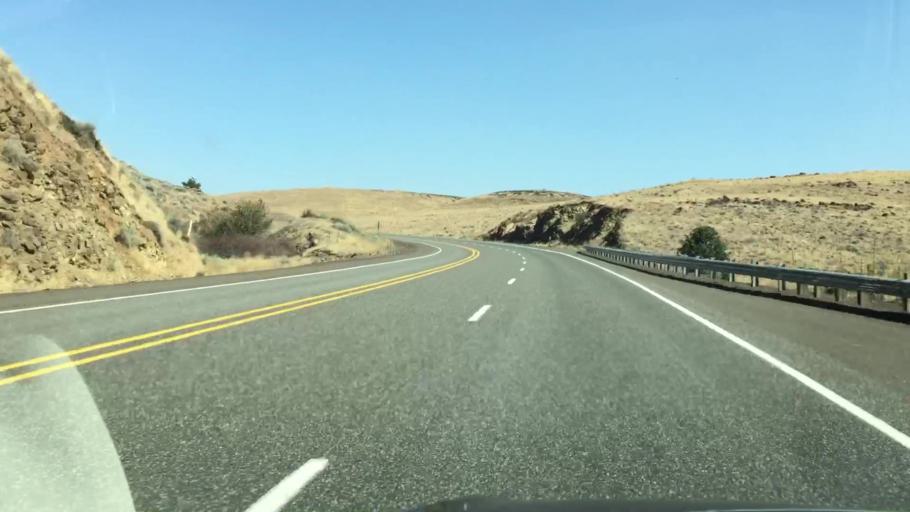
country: US
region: Oregon
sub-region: Wasco County
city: The Dalles
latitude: 45.3121
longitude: -121.1468
